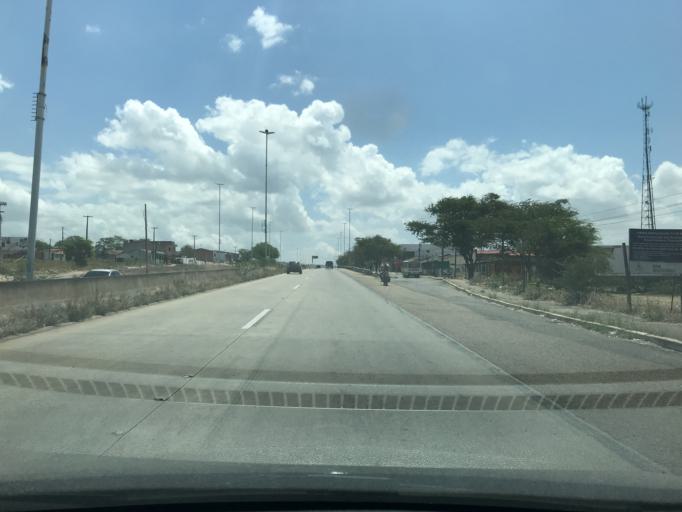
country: BR
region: Pernambuco
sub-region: Bezerros
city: Bezerros
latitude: -8.2993
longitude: -35.8411
